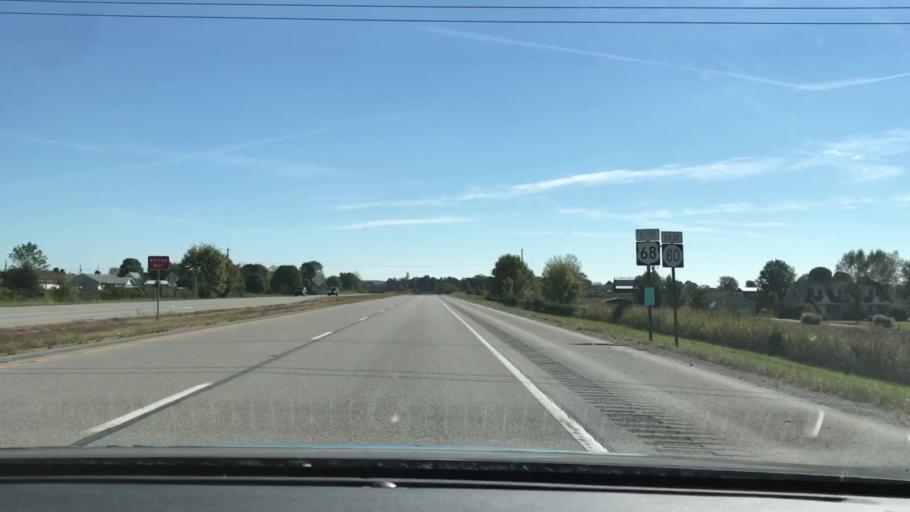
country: US
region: Kentucky
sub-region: Todd County
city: Elkton
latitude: 36.8226
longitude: -87.1991
